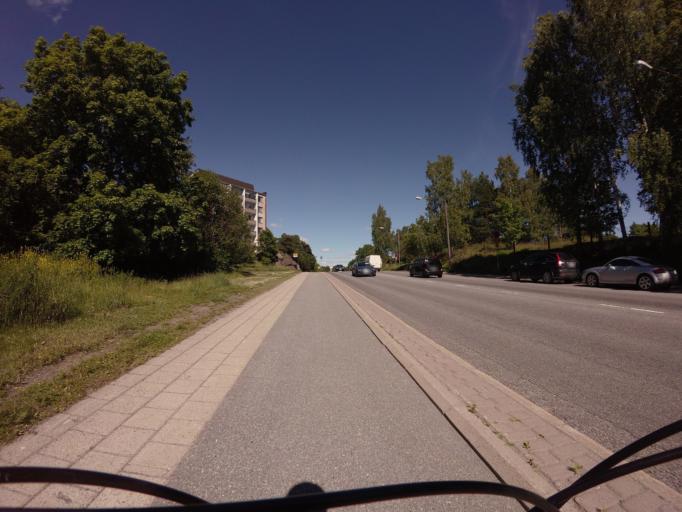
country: FI
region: Varsinais-Suomi
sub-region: Turku
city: Turku
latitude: 60.4586
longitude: 22.2576
